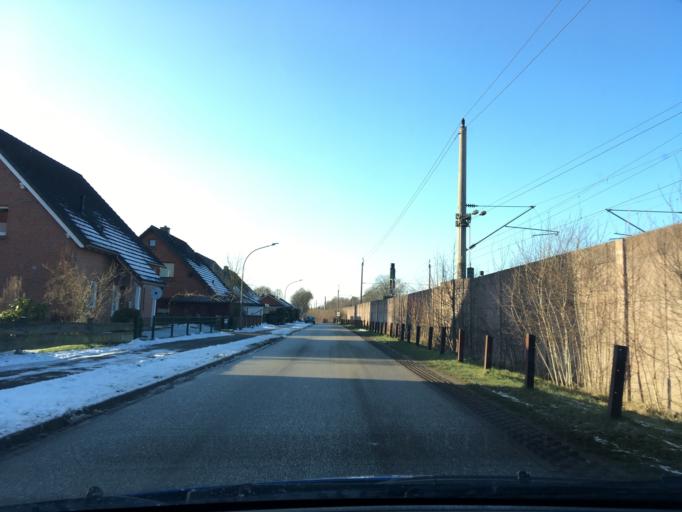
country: DE
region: Schleswig-Holstein
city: Buchen
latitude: 53.4868
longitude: 10.6009
